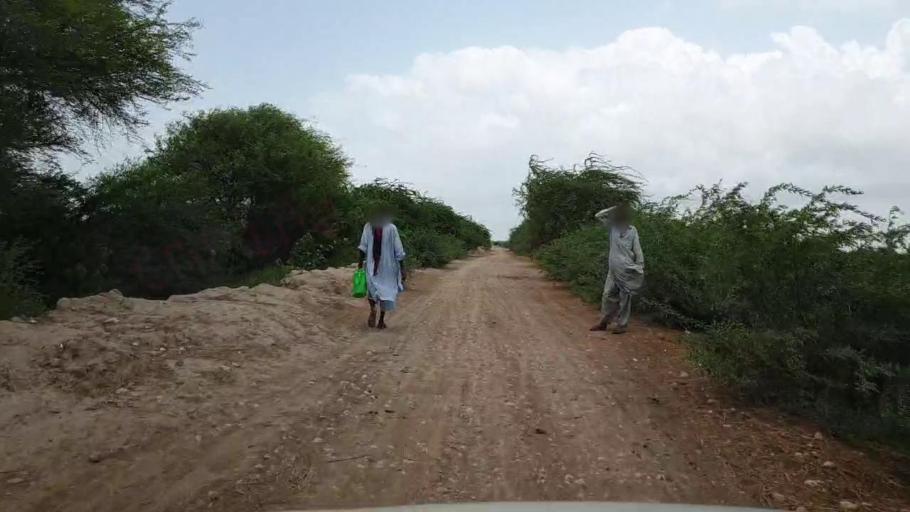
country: PK
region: Sindh
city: Kario
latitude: 24.6915
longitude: 68.6602
